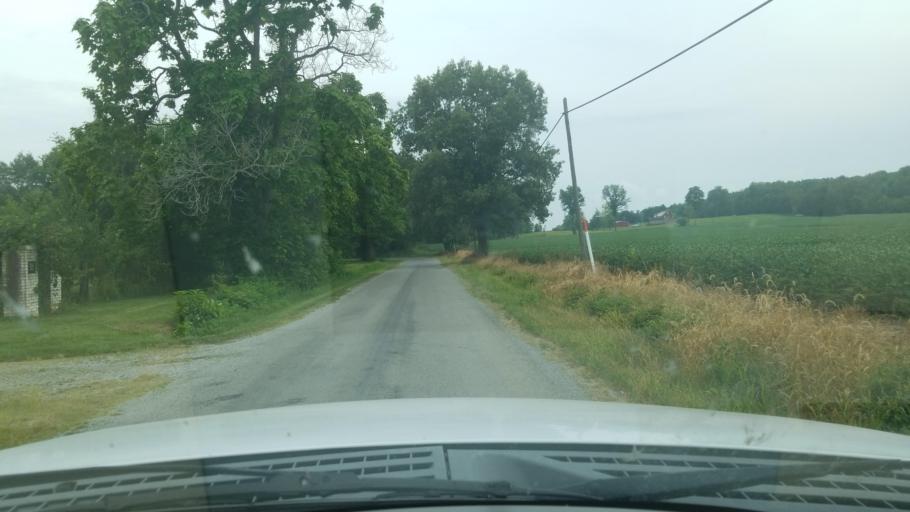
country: US
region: Illinois
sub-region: Saline County
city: Eldorado
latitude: 37.8318
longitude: -88.4502
